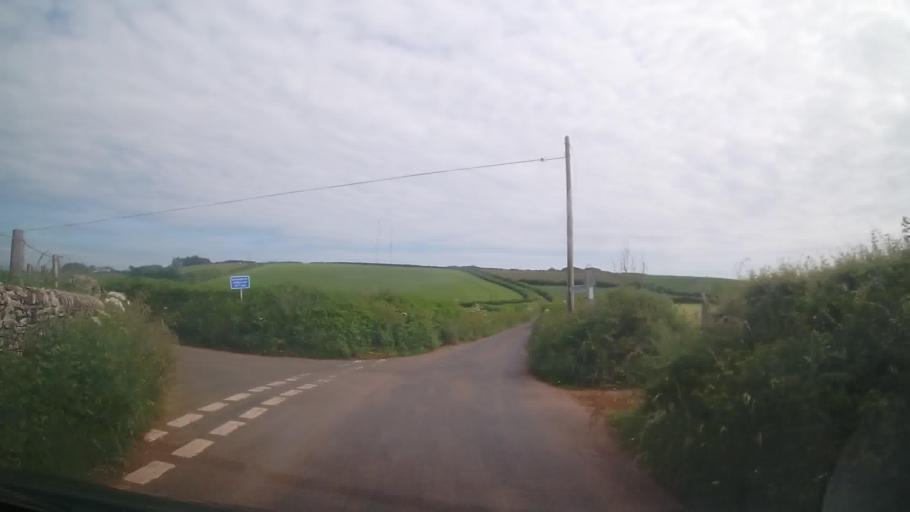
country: GB
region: England
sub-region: Devon
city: Salcombe
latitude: 50.2376
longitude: -3.6749
